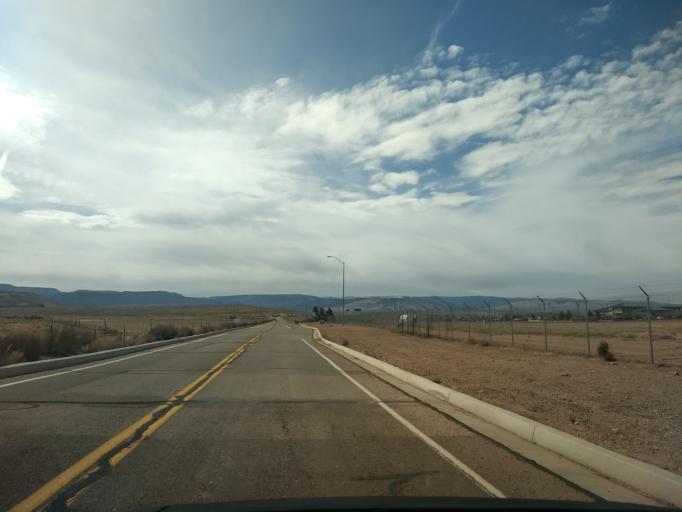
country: US
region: Utah
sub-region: Washington County
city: Washington
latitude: 37.0332
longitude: -113.5039
